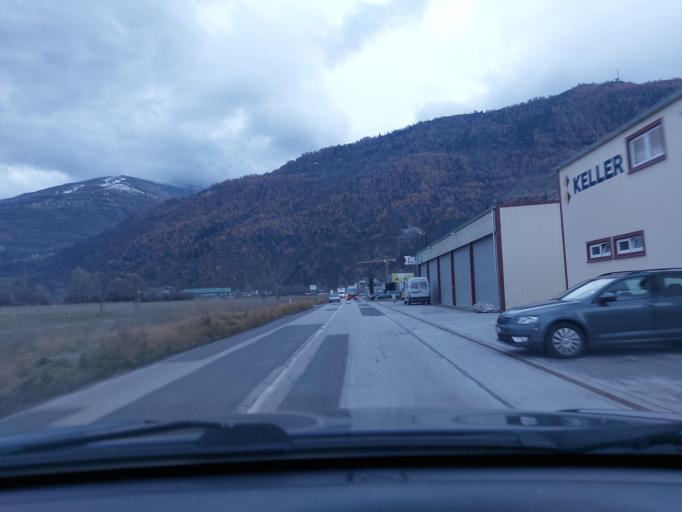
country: CH
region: Valais
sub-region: Conthey District
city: Vetroz
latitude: 46.2066
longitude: 7.2822
